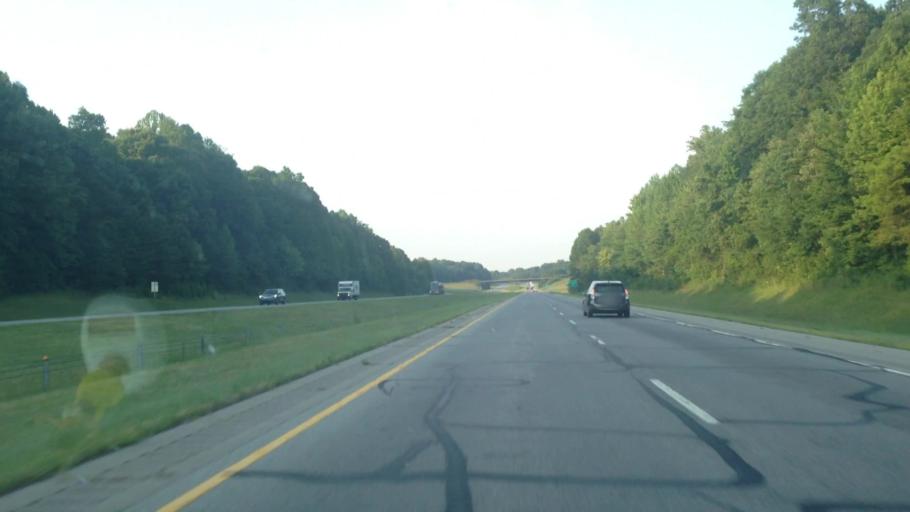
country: US
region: Virginia
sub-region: City of Danville
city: Danville
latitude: 36.4809
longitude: -79.4984
